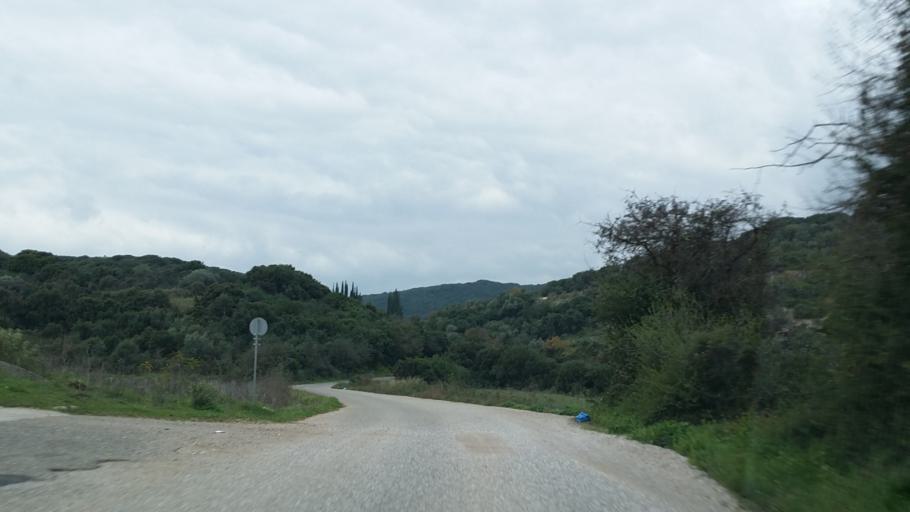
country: GR
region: West Greece
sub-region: Nomos Aitolias kai Akarnanias
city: Fitiai
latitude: 38.7190
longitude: 21.1766
